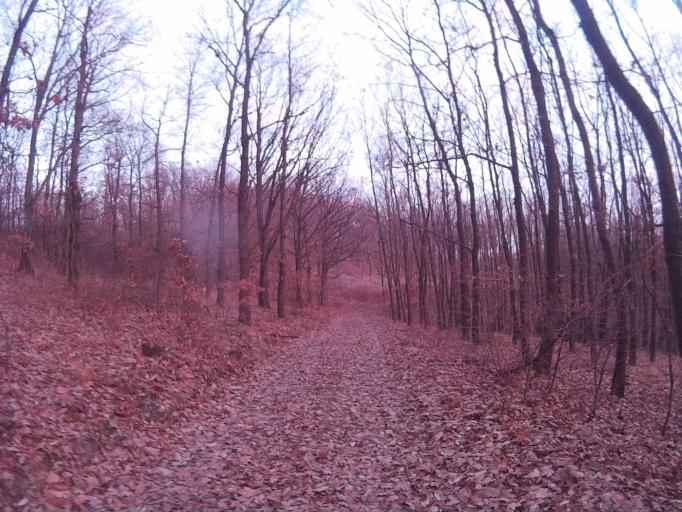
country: HU
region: Nograd
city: Rimoc
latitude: 48.0022
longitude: 19.4520
